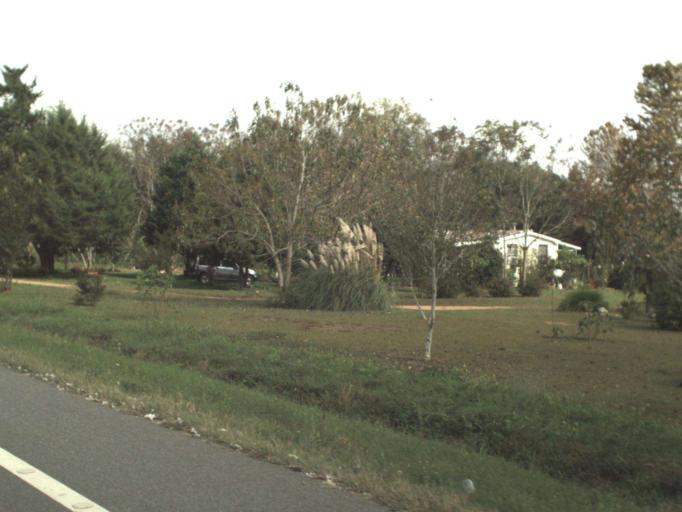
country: US
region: Florida
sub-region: Escambia County
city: Century
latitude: 30.9322
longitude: -87.1573
